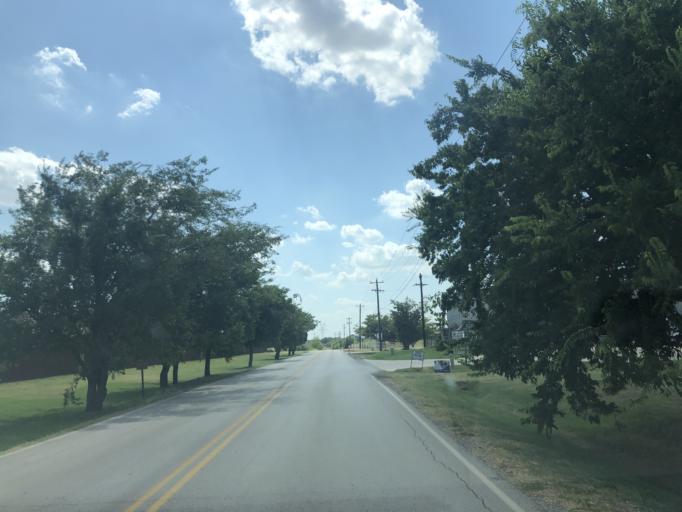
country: US
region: Texas
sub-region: Tarrant County
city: Haslet
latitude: 32.9313
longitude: -97.3266
